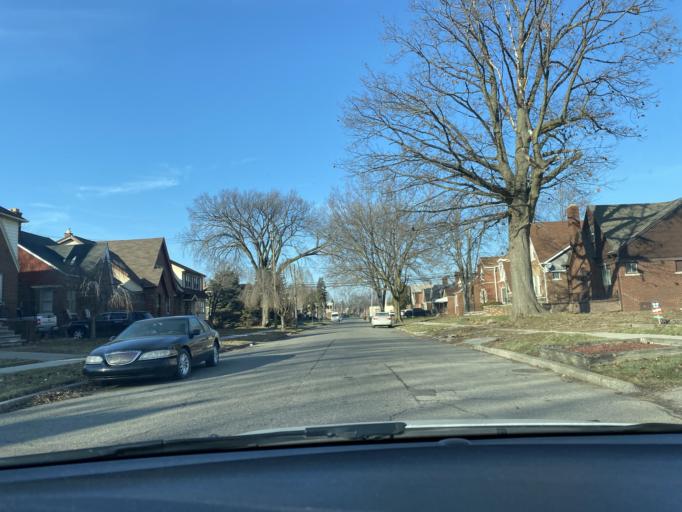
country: US
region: Michigan
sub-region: Wayne County
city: Harper Woods
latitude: 42.4080
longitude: -82.9449
